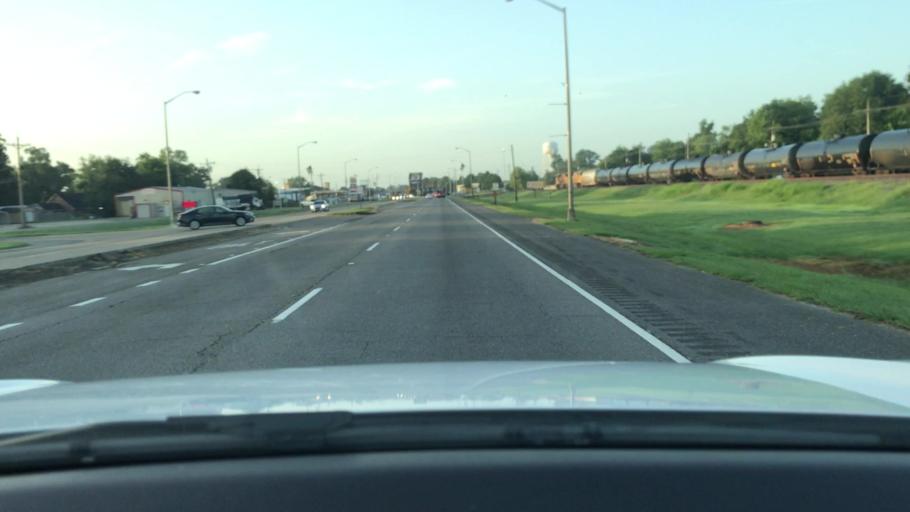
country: US
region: Louisiana
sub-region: Iberville Parish
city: Plaquemine
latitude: 30.3003
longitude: -91.2427
